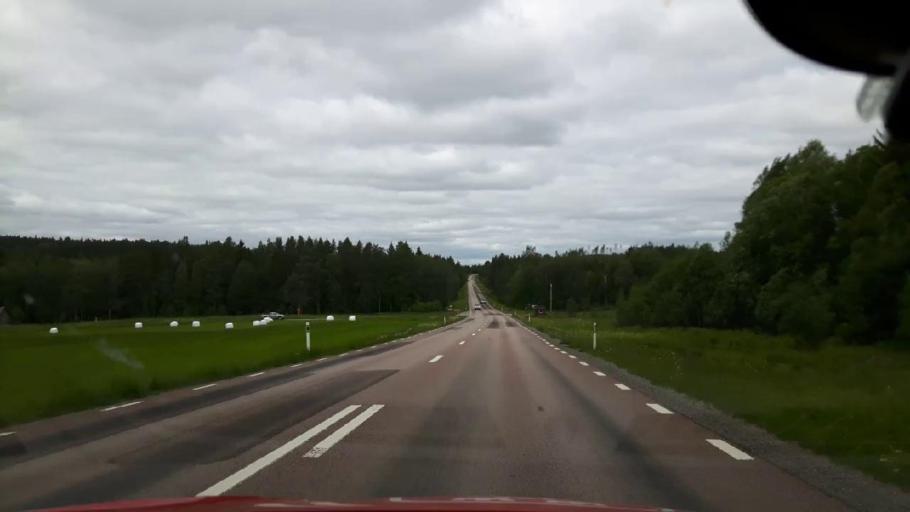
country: SE
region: Jaemtland
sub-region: OEstersunds Kommun
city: Brunflo
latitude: 62.9884
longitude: 14.9861
